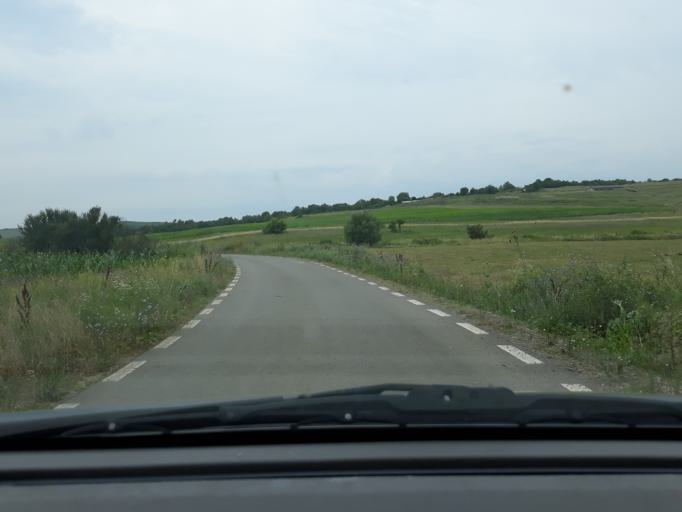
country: RO
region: Salaj
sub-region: Comuna Criseni
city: Criseni
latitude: 47.2682
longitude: 23.0674
